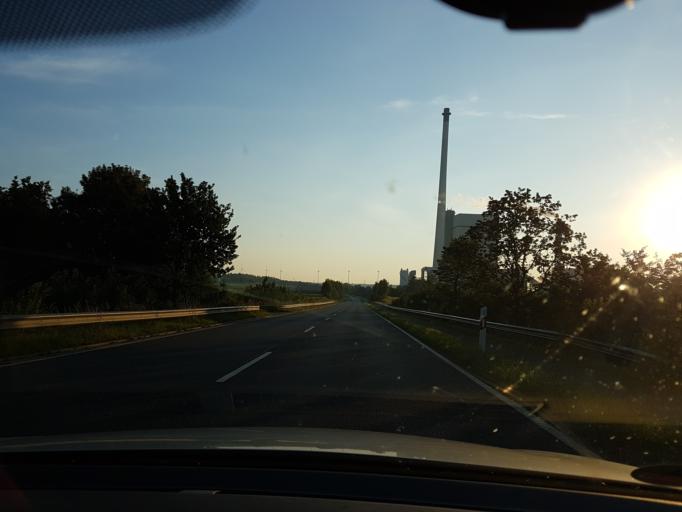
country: DE
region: Lower Saxony
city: Schoningen
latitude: 52.1658
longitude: 10.9695
